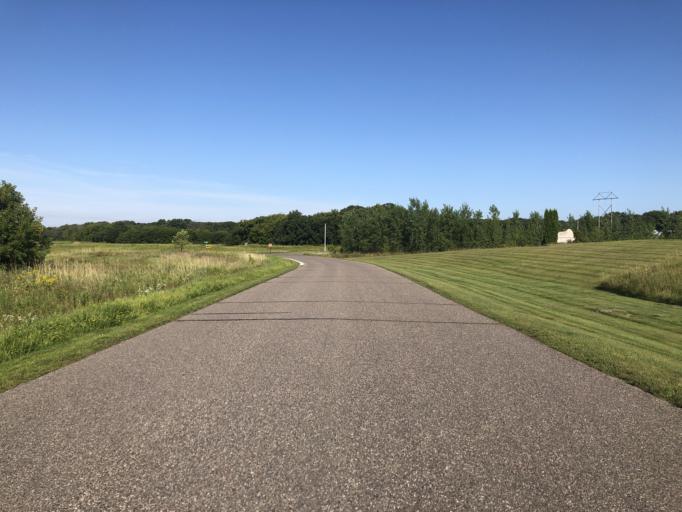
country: US
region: Minnesota
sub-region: Sherburne County
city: Becker
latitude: 45.4239
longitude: -93.8384
